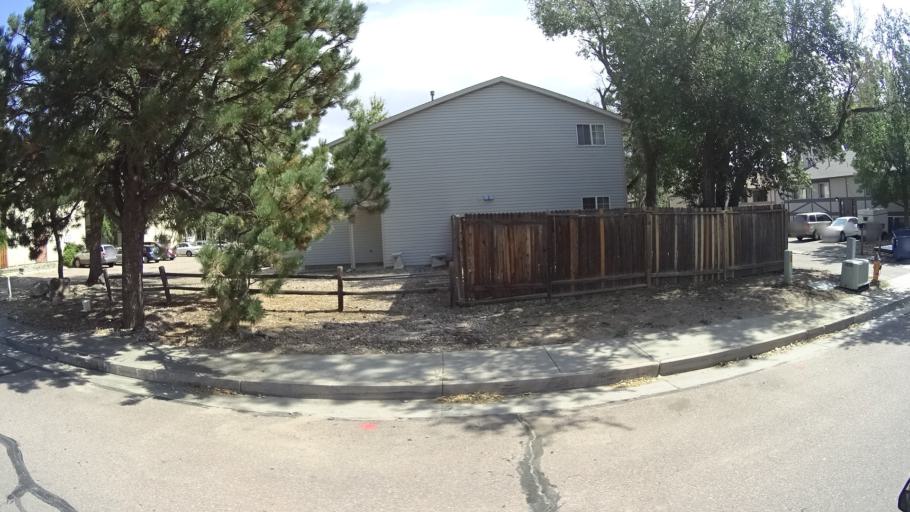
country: US
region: Colorado
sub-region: El Paso County
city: Cimarron Hills
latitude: 38.8584
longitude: -104.7260
